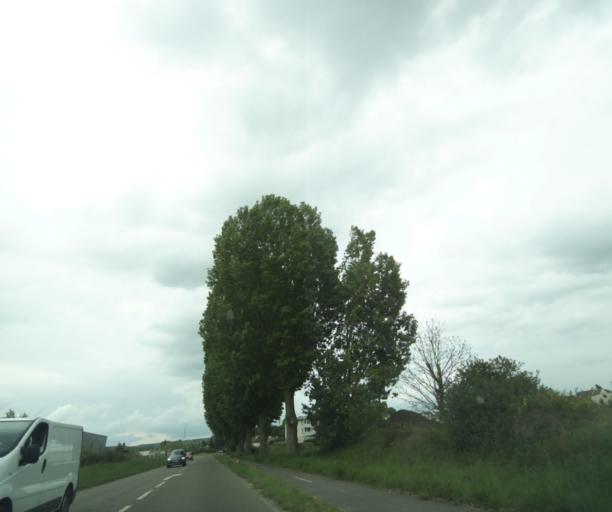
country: FR
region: Ile-de-France
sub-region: Departement des Yvelines
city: Ecquevilly
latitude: 48.9560
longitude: 1.9262
